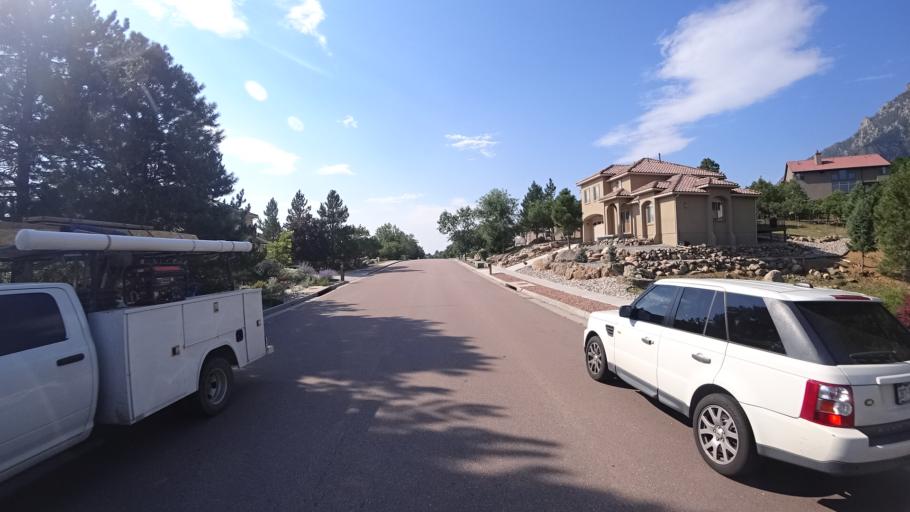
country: US
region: Colorado
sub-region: El Paso County
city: Fort Carson
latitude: 38.7524
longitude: -104.8334
